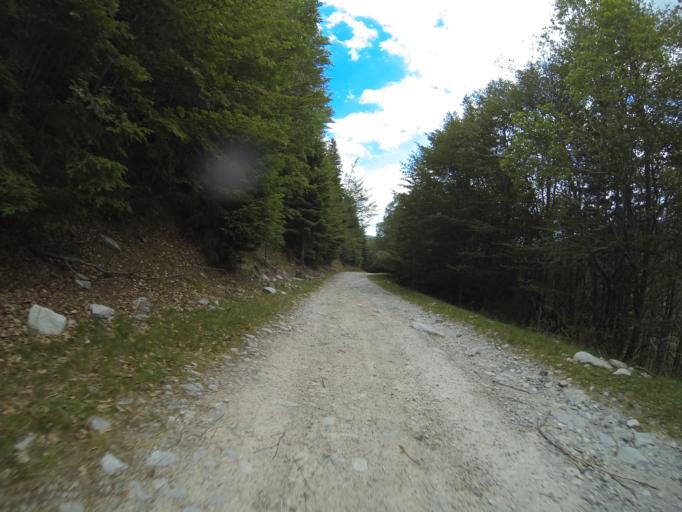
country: RO
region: Gorj
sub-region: Comuna Polovragi
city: Polovragi
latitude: 45.3332
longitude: 23.7953
